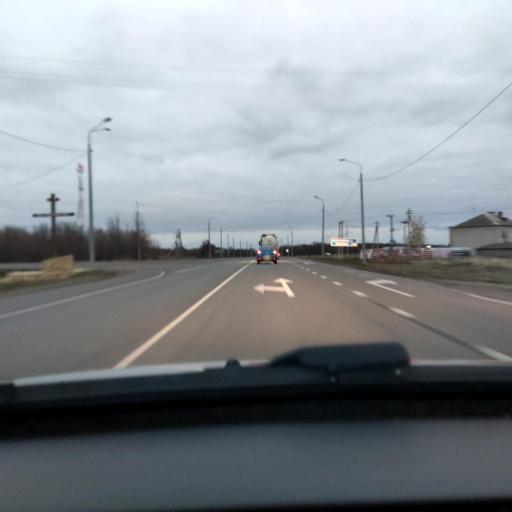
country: RU
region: Lipetsk
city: Borinskoye
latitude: 52.4620
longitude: 39.3281
